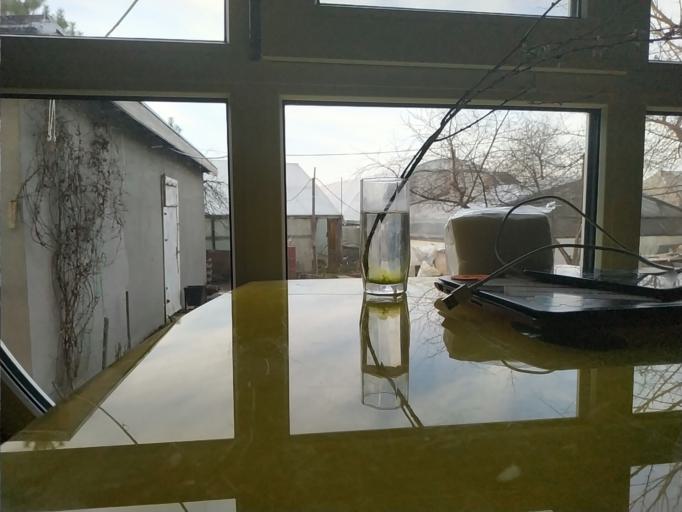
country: RU
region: Republic of Karelia
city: Suoyarvi
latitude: 61.9194
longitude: 32.2465
